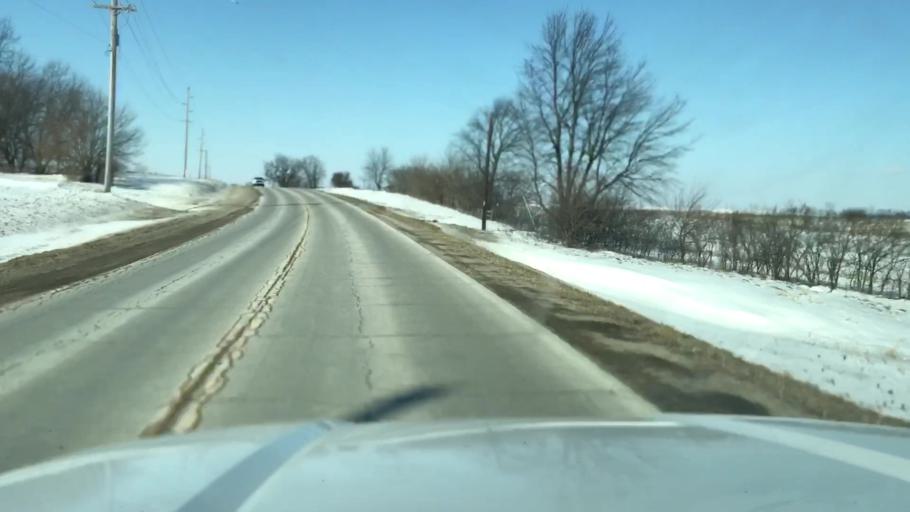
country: US
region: Missouri
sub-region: Andrew County
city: Savannah
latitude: 39.9590
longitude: -94.8523
